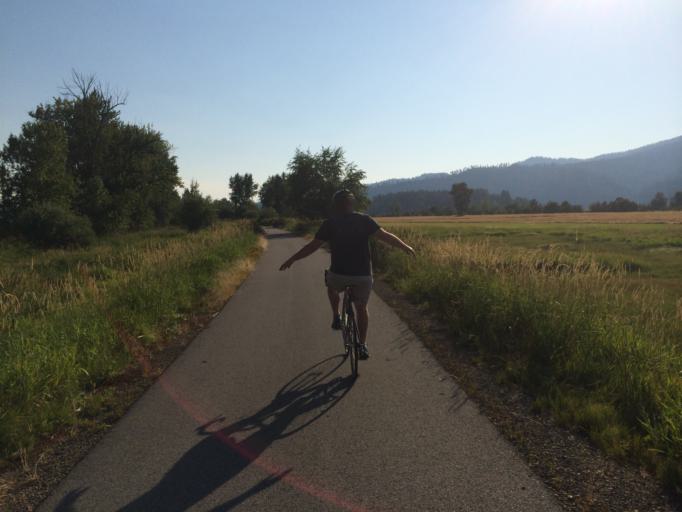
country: US
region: Idaho
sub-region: Benewah County
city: Saint Maries
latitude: 47.5035
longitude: -116.5572
